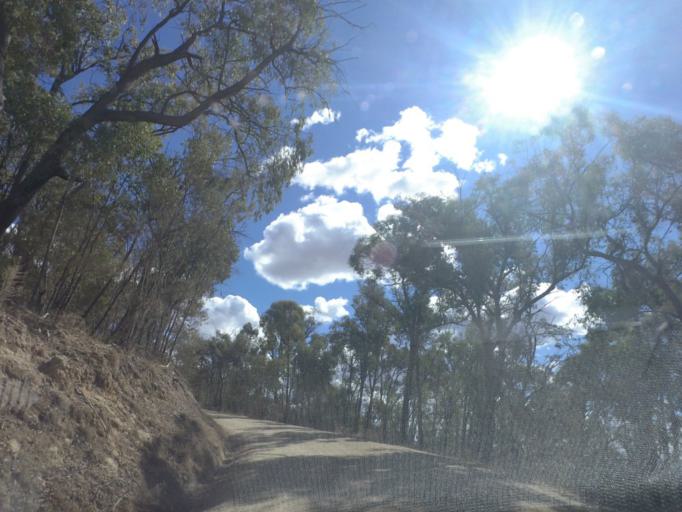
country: AU
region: Victoria
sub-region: Murrindindi
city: Alexandra
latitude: -37.3224
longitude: 145.8088
